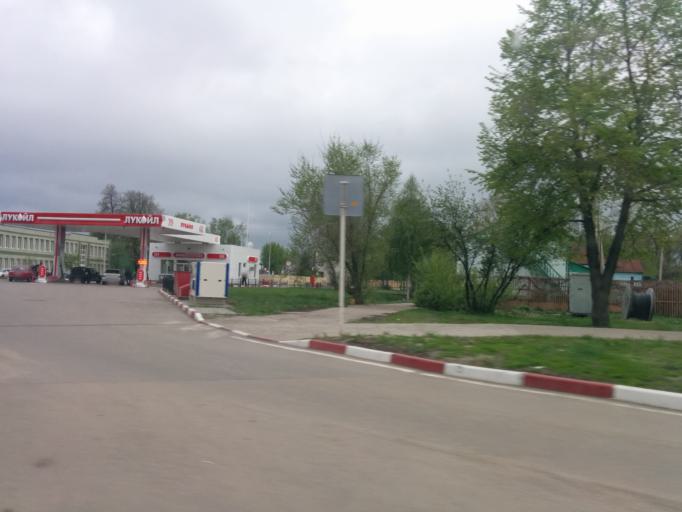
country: RU
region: Tambov
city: Tambov
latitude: 52.7263
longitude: 41.4357
